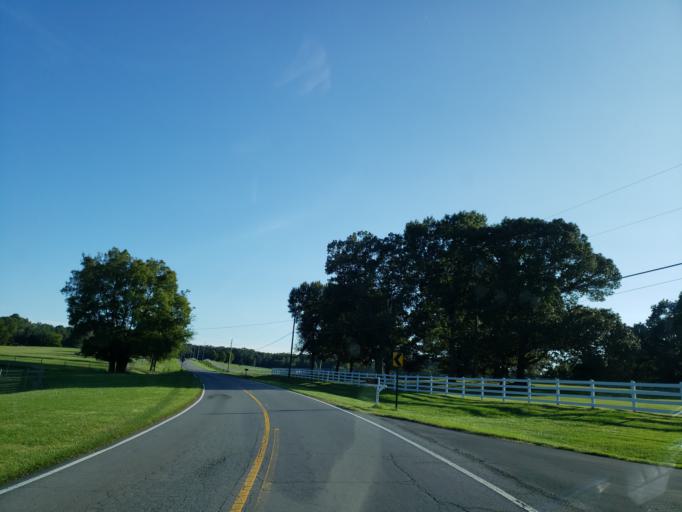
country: US
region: Georgia
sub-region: Bartow County
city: Rydal
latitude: 34.3121
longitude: -84.7739
